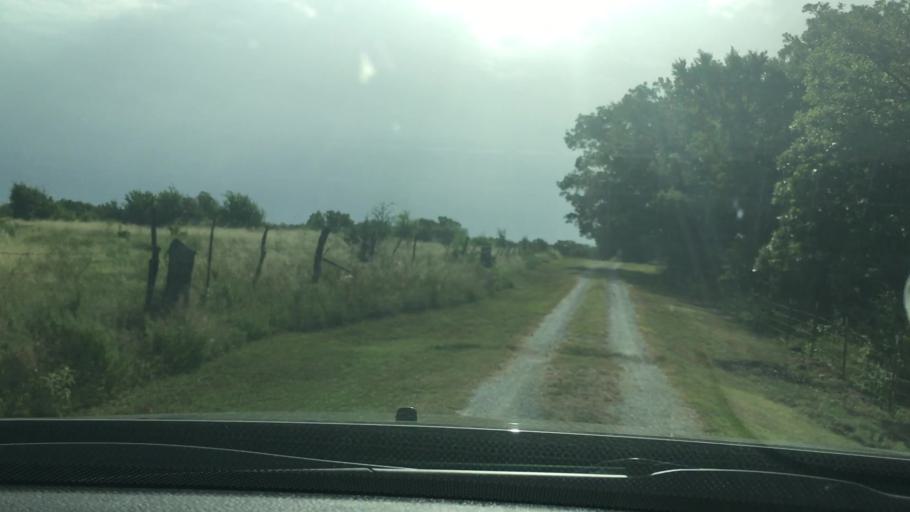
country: US
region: Oklahoma
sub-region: Pontotoc County
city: Byng
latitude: 34.8647
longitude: -96.5712
